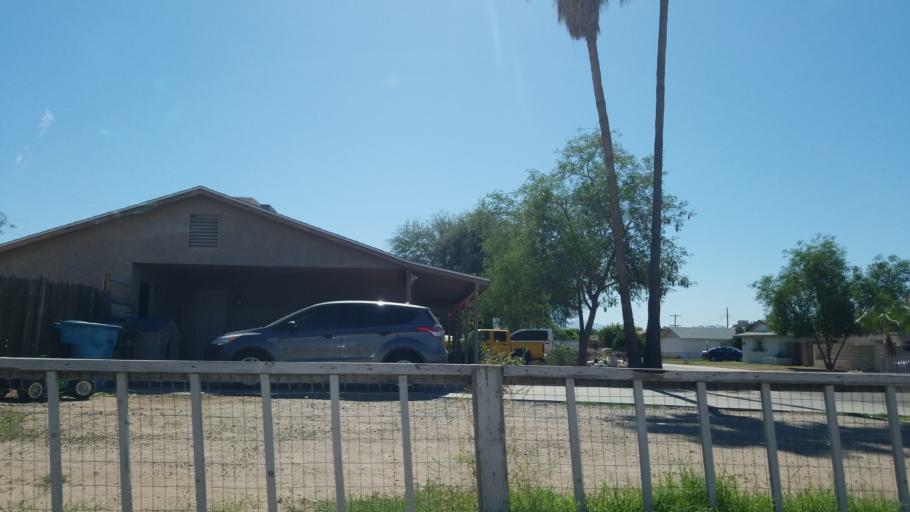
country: US
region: Arizona
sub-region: Maricopa County
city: Tolleson
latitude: 33.4871
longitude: -112.2317
